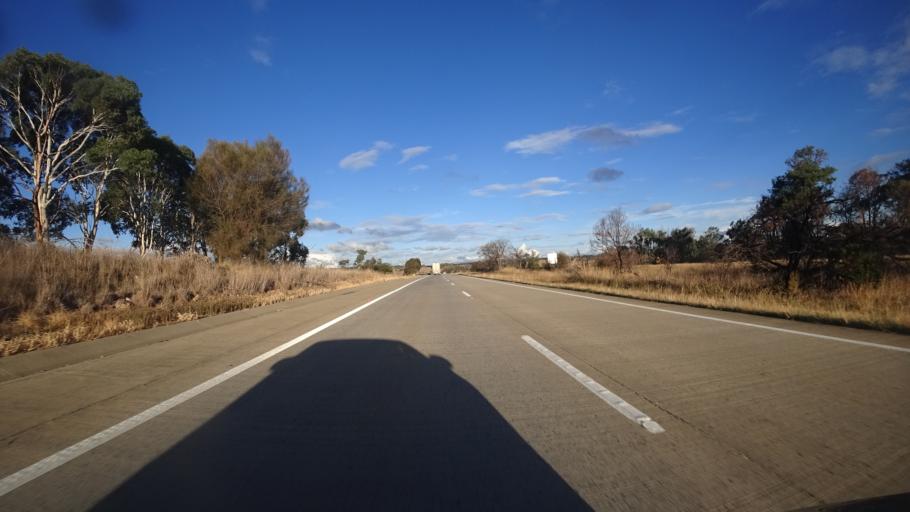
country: AU
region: New South Wales
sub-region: Yass Valley
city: Gundaroo
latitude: -34.8016
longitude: 149.2961
